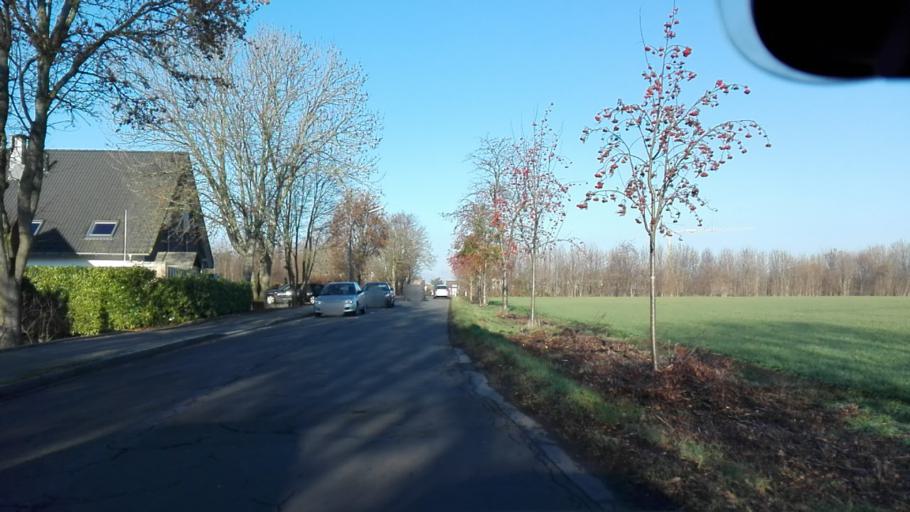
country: DE
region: North Rhine-Westphalia
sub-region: Regierungsbezirk Arnsberg
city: Holzwickede
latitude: 51.5139
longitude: 7.6282
